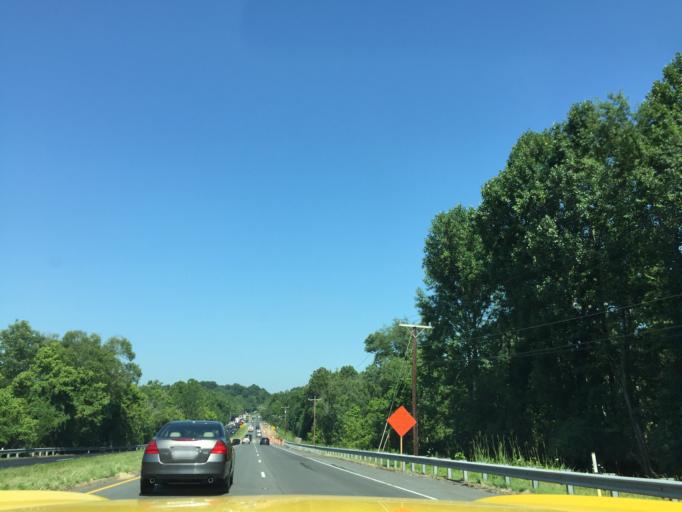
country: US
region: Virginia
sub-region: Fairfax County
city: Wolf Trap
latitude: 38.9655
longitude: -77.2860
